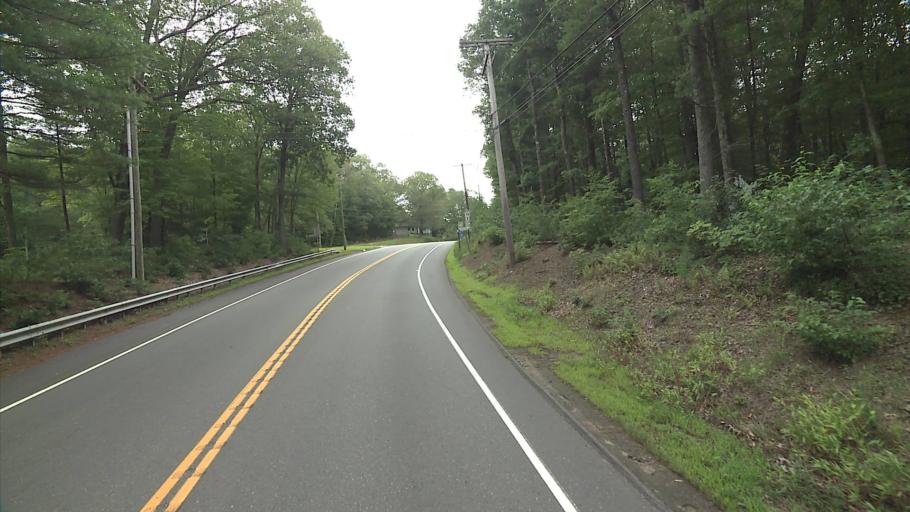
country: US
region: Connecticut
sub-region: Tolland County
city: Storrs
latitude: 41.8770
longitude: -72.2684
